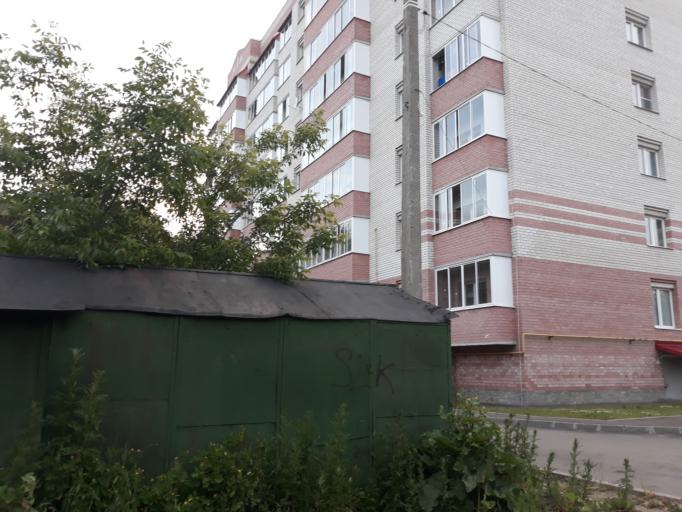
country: RU
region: Jaroslavl
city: Yaroslavl
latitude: 57.6415
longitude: 39.8315
